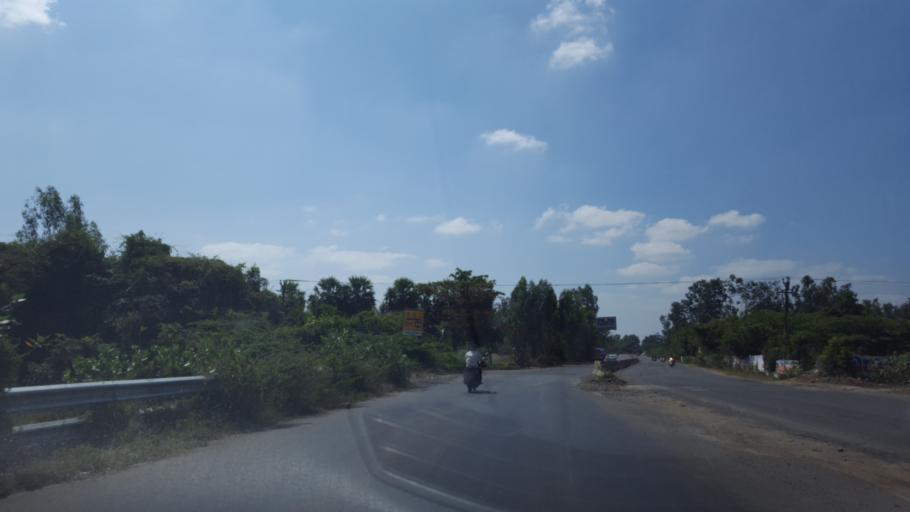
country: IN
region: Tamil Nadu
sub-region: Kancheepuram
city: Mamallapuram
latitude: 12.7032
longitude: 80.1836
